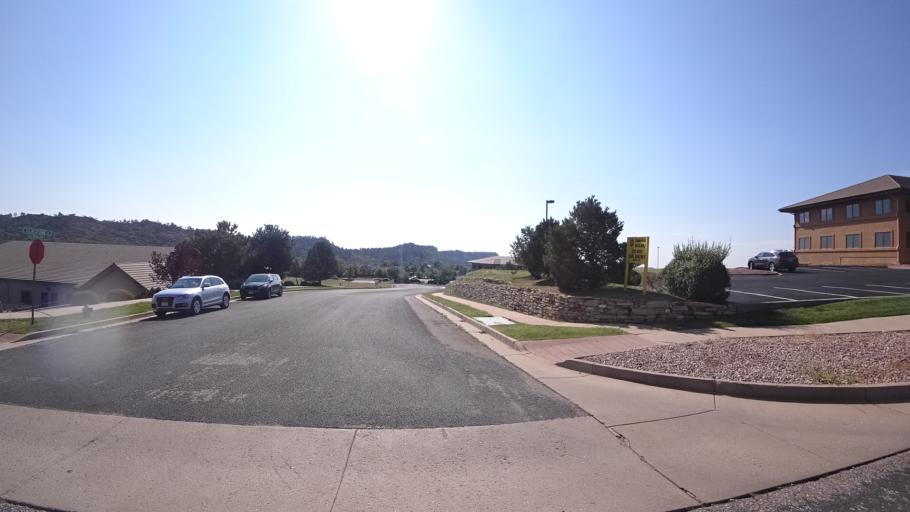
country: US
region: Colorado
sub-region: El Paso County
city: Manitou Springs
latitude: 38.9151
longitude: -104.8656
